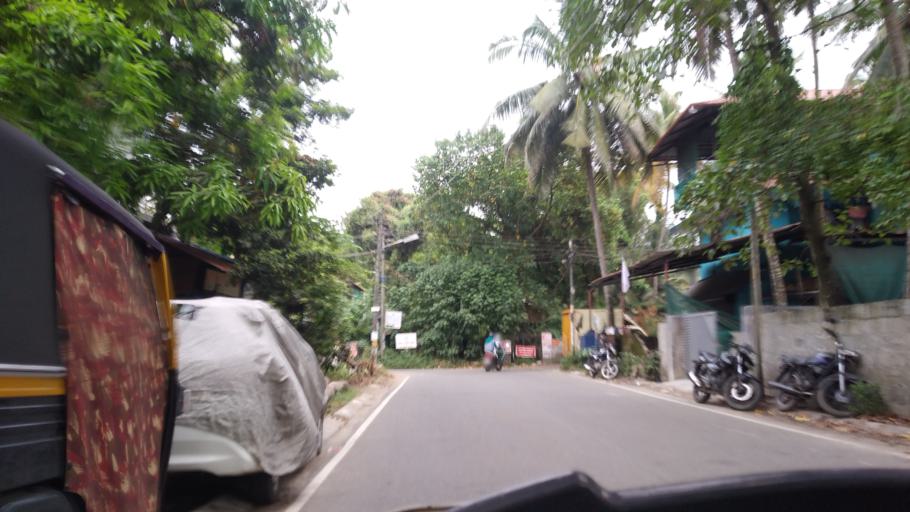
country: IN
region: Kerala
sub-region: Ernakulam
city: Cochin
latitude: 9.9549
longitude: 76.3162
